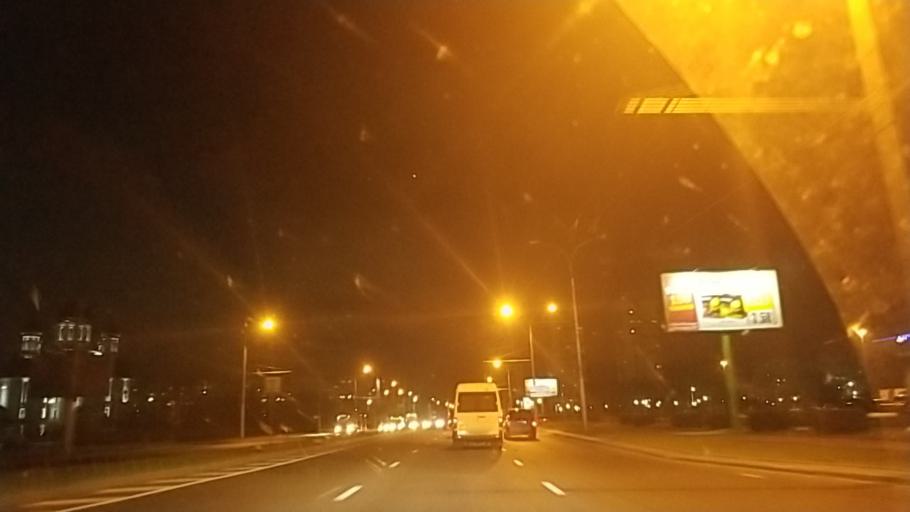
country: BY
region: Brest
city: Brest
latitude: 52.0967
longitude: 23.7655
